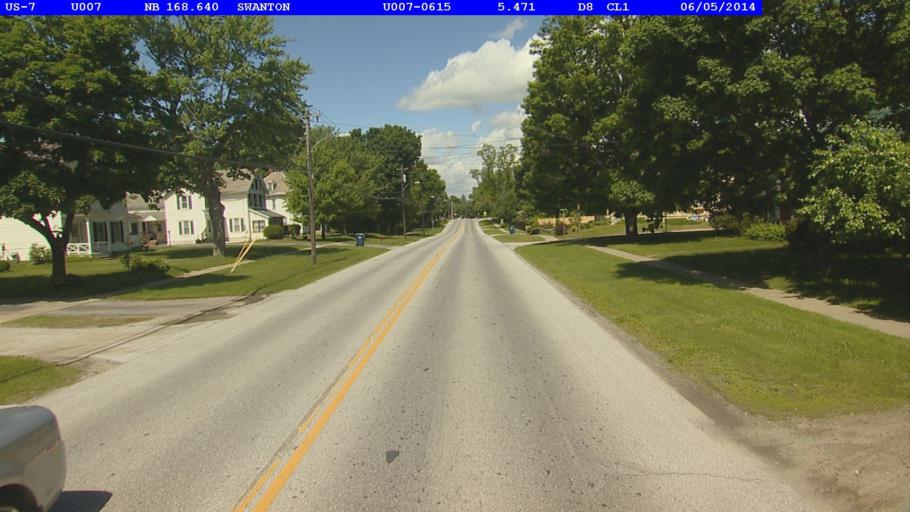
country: US
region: Vermont
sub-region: Franklin County
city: Swanton
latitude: 44.9156
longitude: -73.1194
